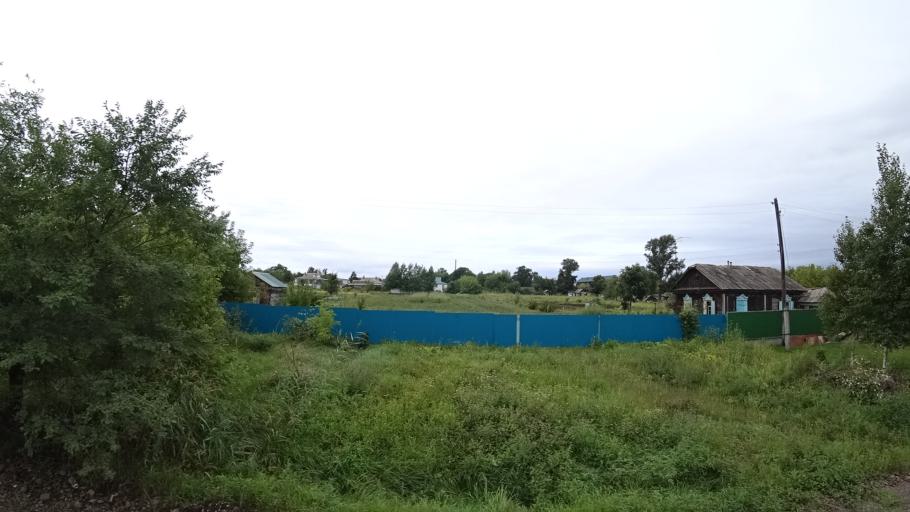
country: RU
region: Primorskiy
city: Chernigovka
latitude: 44.3345
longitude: 132.5674
